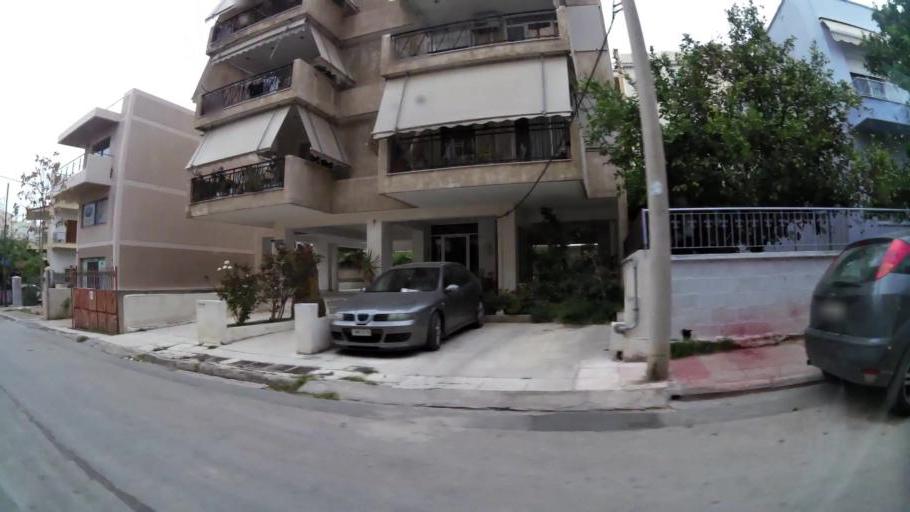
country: GR
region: Attica
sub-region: Nomarchia Athinas
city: Ilion
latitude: 38.0291
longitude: 23.7100
